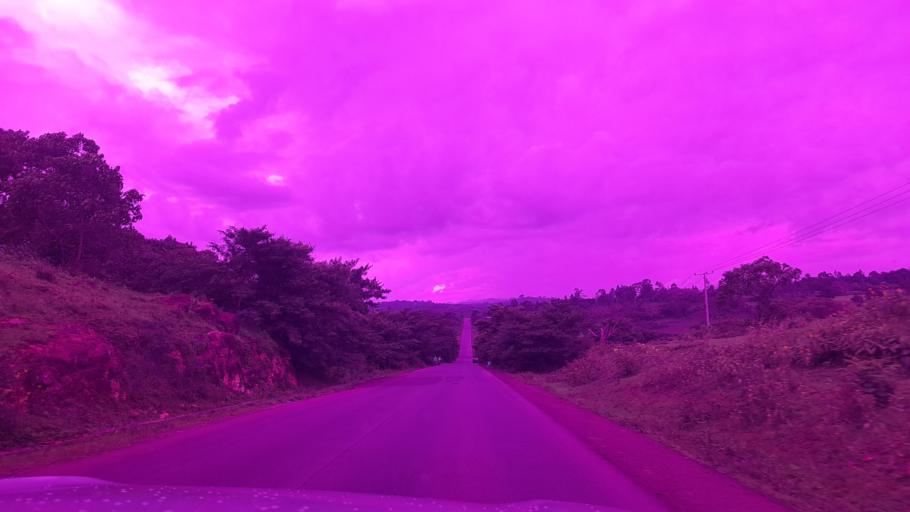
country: ET
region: Oromiya
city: Jima
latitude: 7.7600
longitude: 37.3353
